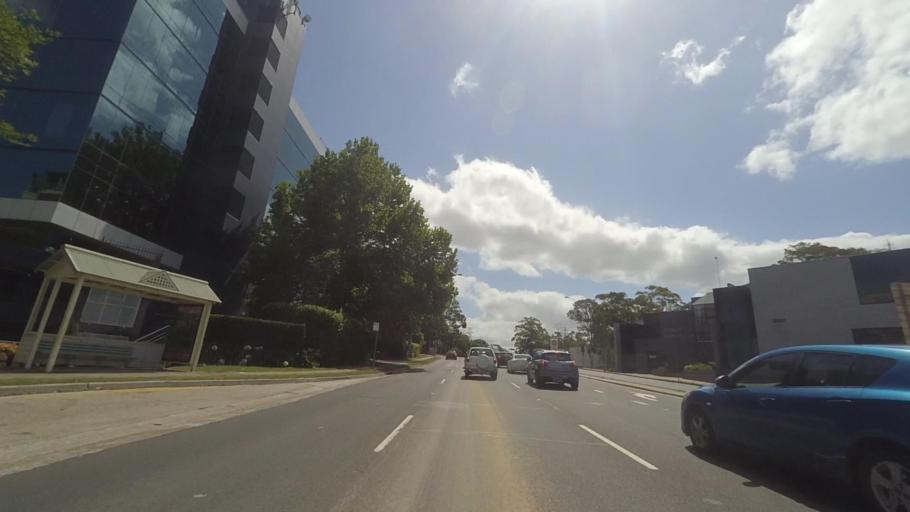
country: AU
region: New South Wales
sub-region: Hornsby Shire
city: Pennant Hills
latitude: -33.7394
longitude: 151.0696
